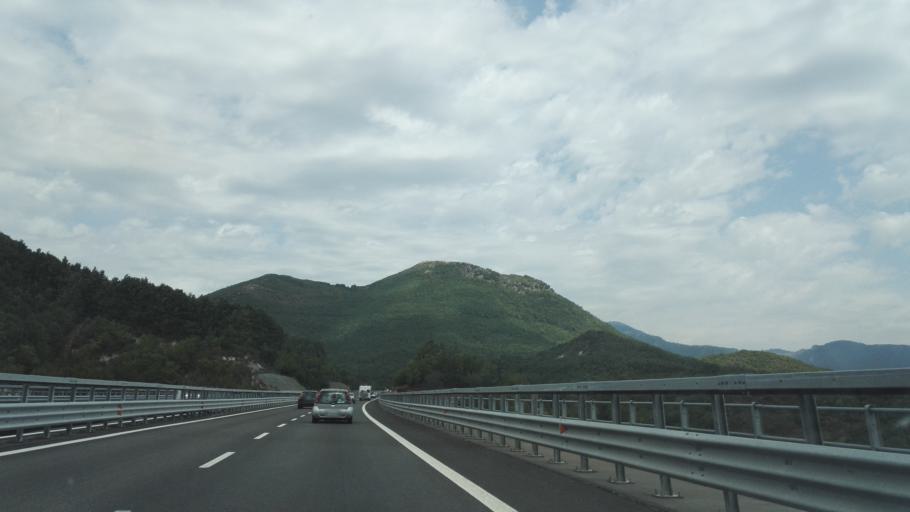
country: IT
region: Calabria
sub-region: Provincia di Cosenza
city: Laino Borgo
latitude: 39.9794
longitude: 15.9353
